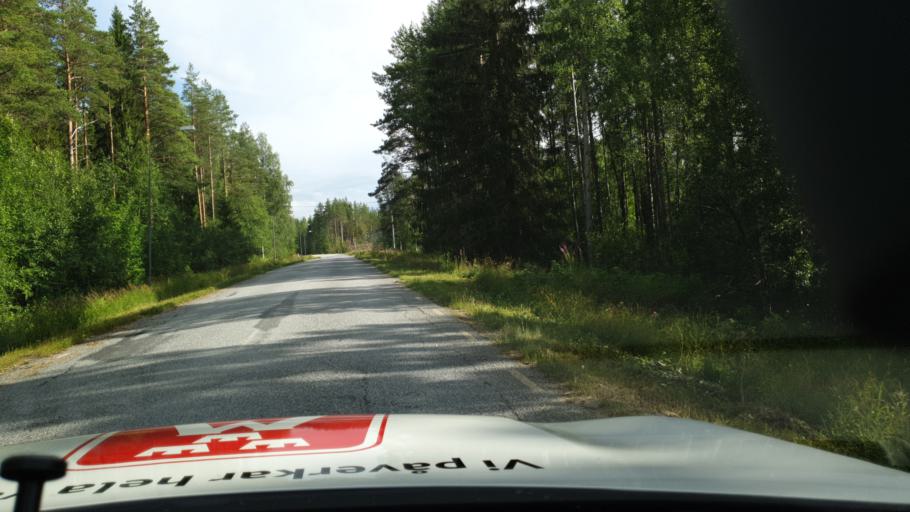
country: SE
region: Vaesterbotten
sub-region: Skelleftea Kommun
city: Burea
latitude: 64.4883
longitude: 21.0342
